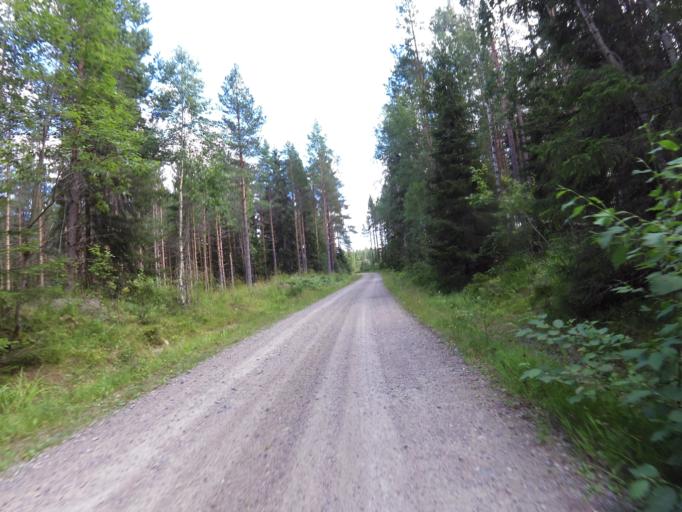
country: SE
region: Gaevleborg
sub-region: Hofors Kommun
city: Hofors
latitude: 60.5226
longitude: 16.2482
